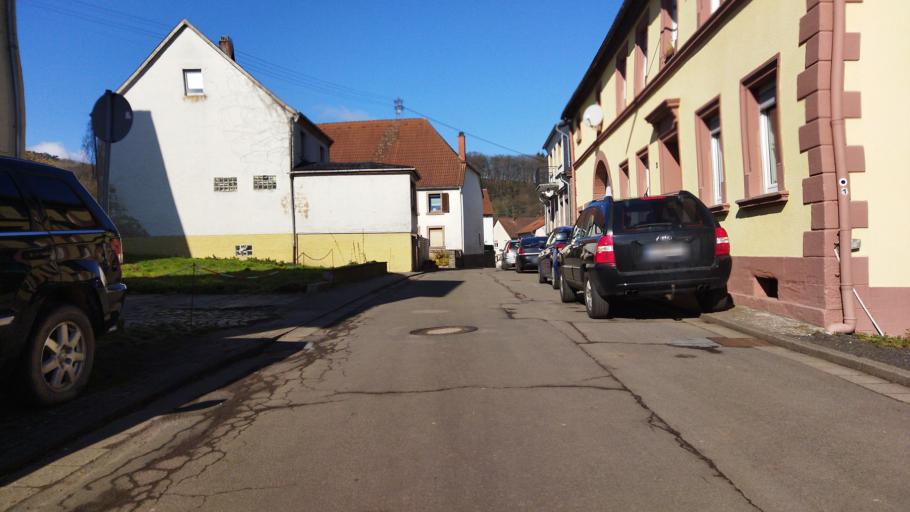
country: DE
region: Rheinland-Pfalz
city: Etschberg
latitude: 49.5114
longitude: 7.4452
